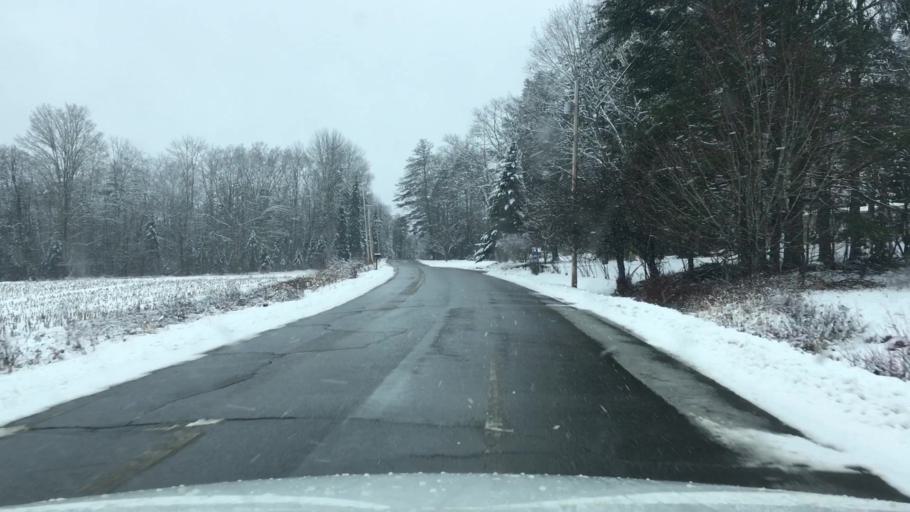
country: US
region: Maine
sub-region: Knox County
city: Union
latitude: 44.1706
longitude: -69.3254
